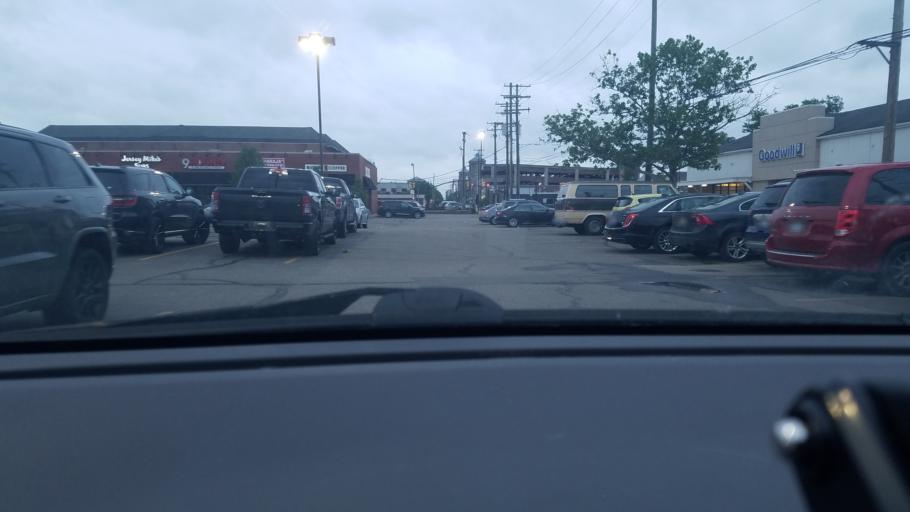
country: US
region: Michigan
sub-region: Wayne County
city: Dearborn Heights
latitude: 42.3036
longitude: -83.2527
